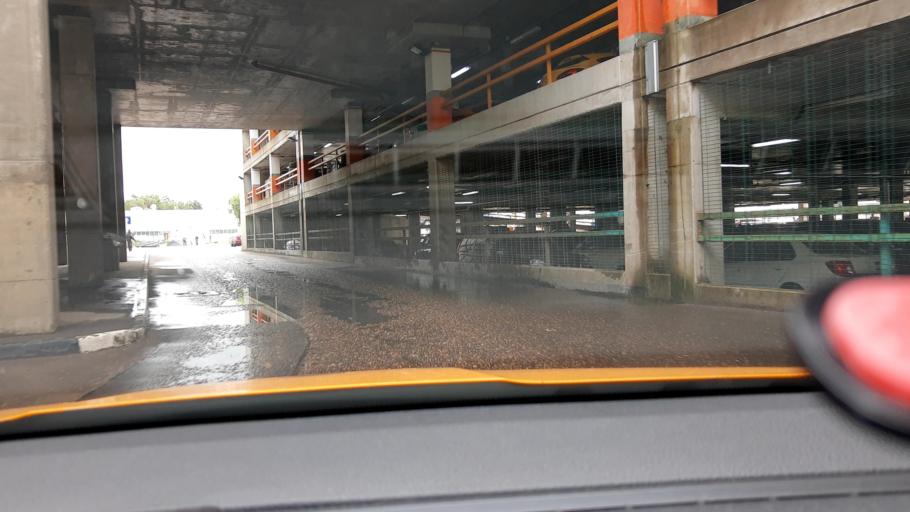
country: RU
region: Moskovskaya
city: Opalikha
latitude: 55.7908
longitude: 37.2542
